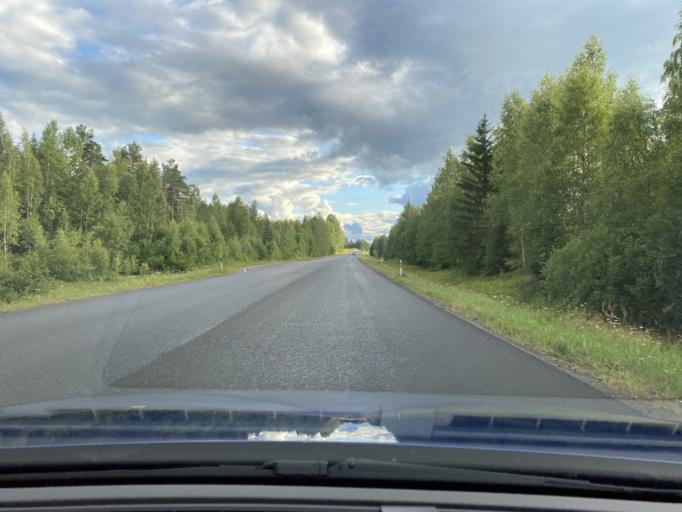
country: FI
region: Haeme
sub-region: Haemeenlinna
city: Renko
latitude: 60.9165
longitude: 24.3268
